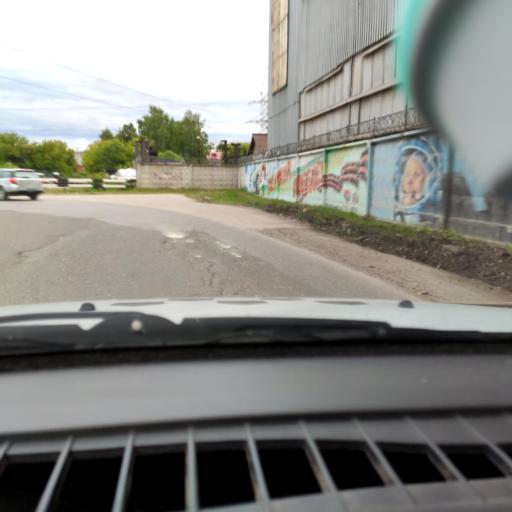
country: RU
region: Perm
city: Chusovoy
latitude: 58.2915
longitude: 57.8171
